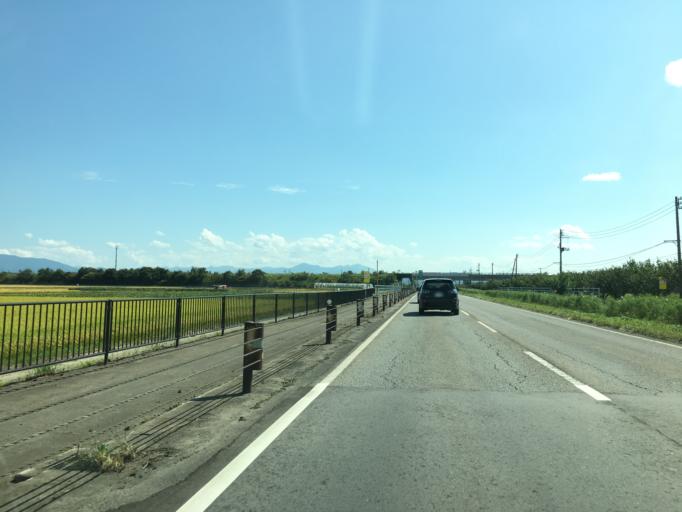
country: JP
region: Niigata
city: Niitsu-honcho
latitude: 37.8239
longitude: 139.0985
